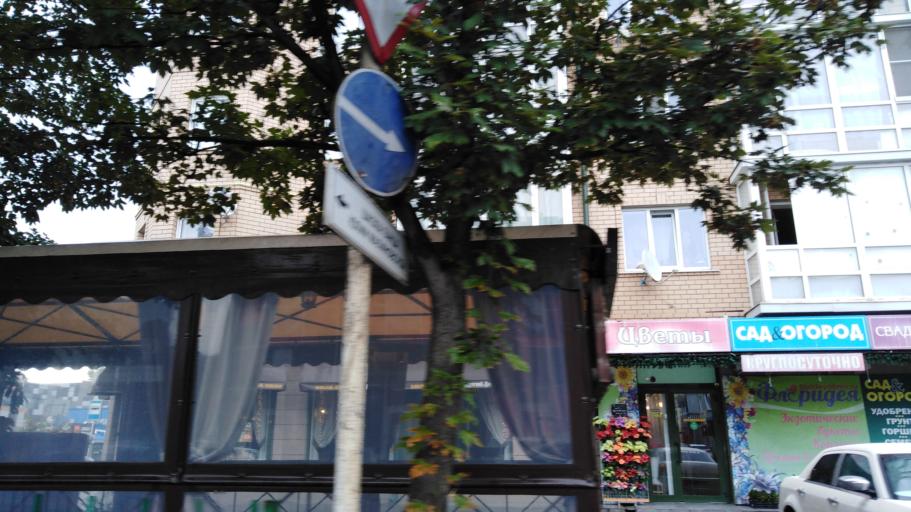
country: RU
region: Stavropol'skiy
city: Yessentukskaya
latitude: 44.0494
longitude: 42.8952
